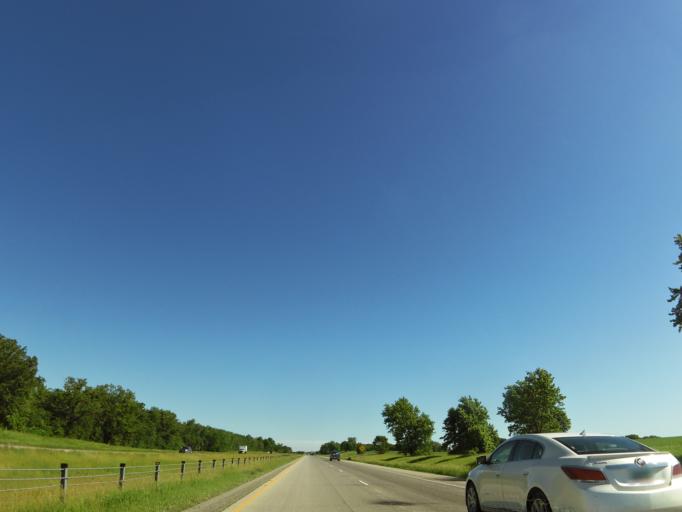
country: US
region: Minnesota
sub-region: Otter Tail County
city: Fergus Falls
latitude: 46.3194
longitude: -96.1225
